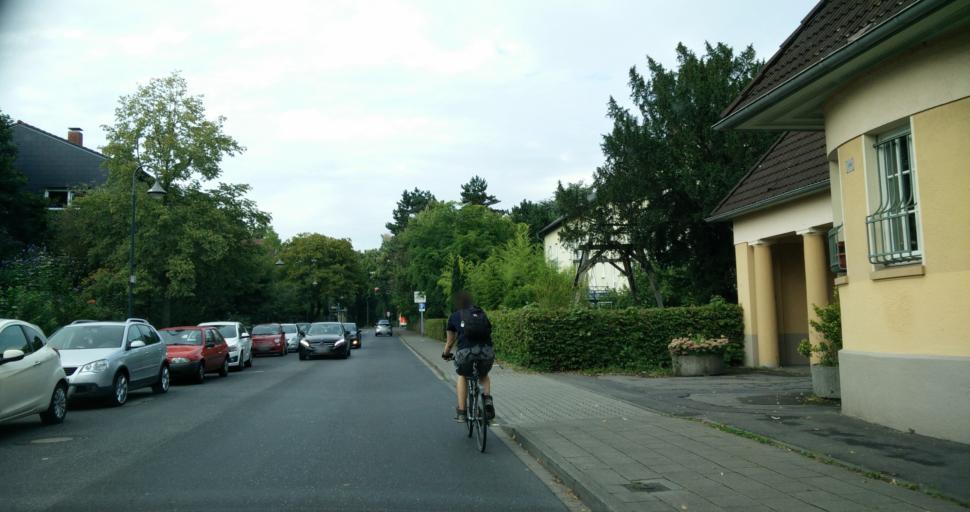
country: DE
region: North Rhine-Westphalia
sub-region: Regierungsbezirk Dusseldorf
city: Meerbusch
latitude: 51.2978
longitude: 6.7421
